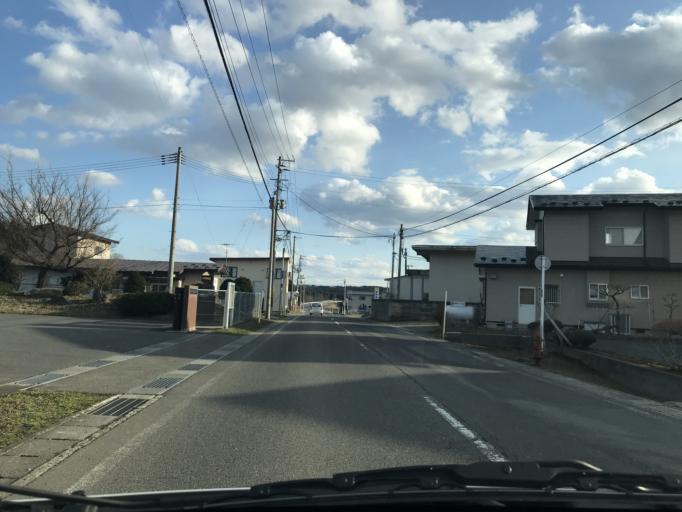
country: JP
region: Iwate
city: Kitakami
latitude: 39.2974
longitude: 141.0324
